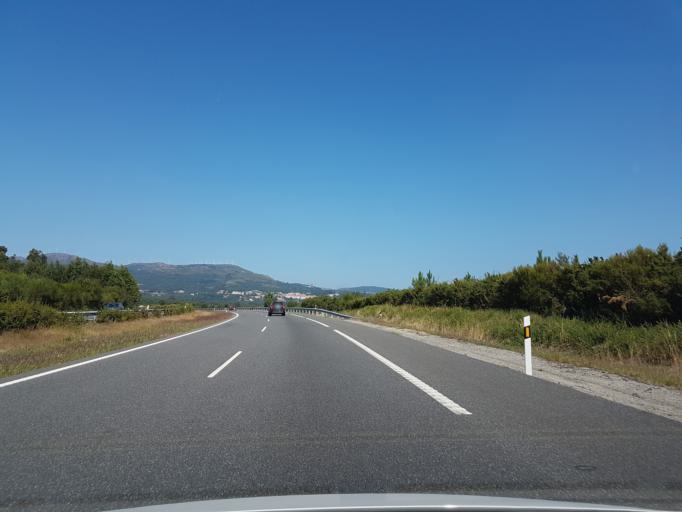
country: ES
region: Galicia
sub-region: Provincia de Pontevedra
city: Covelo
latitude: 42.1876
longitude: -8.3105
